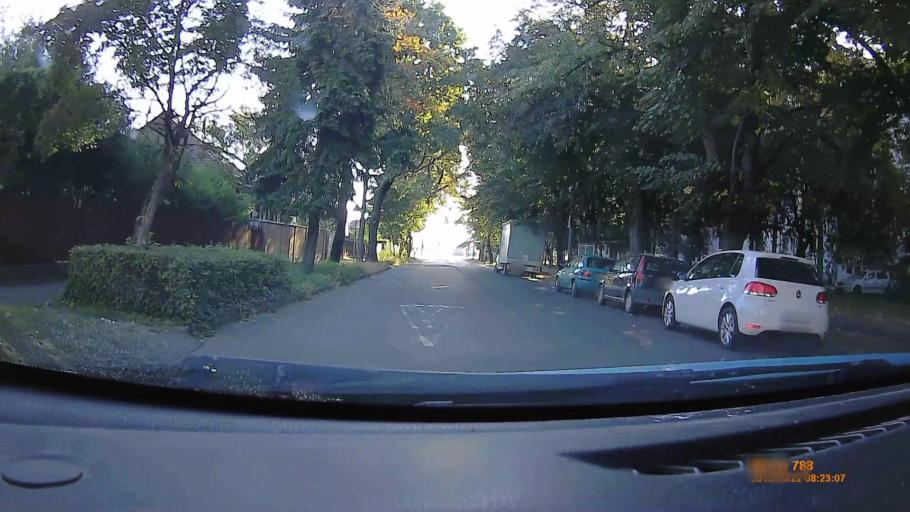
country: HU
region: Borsod-Abauj-Zemplen
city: Sajobabony
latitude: 48.0973
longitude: 20.7086
